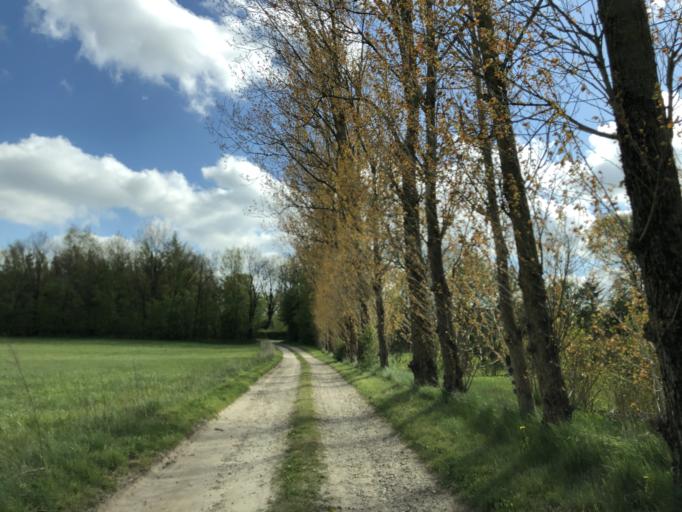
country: DK
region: Central Jutland
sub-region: Herning Kommune
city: Avlum
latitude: 56.3027
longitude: 8.7646
